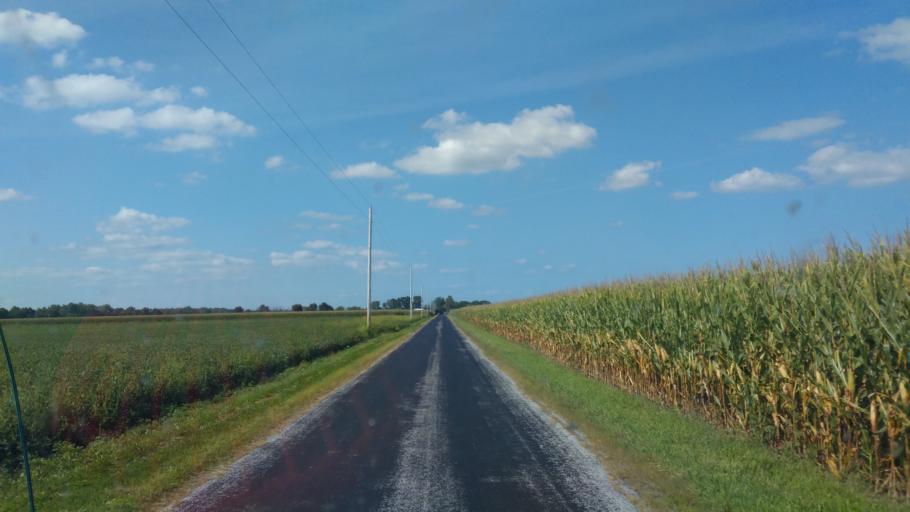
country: US
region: Ohio
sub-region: Hardin County
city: Forest
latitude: 40.7026
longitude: -83.4779
